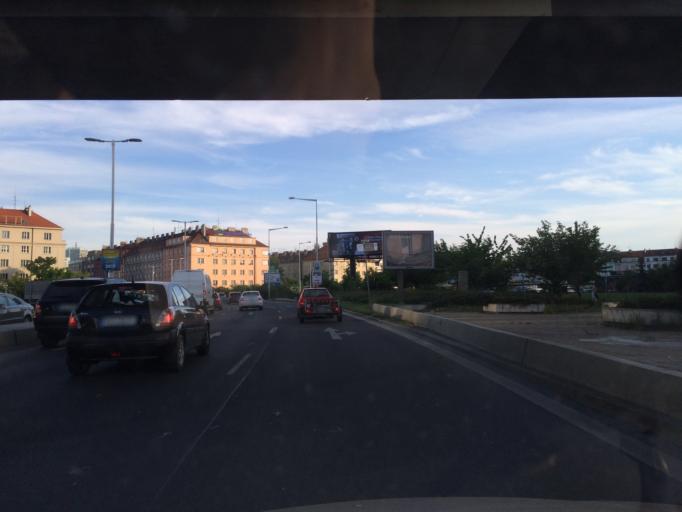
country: CZ
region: Praha
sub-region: Praha 2
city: Vysehrad
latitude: 50.0627
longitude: 14.4304
